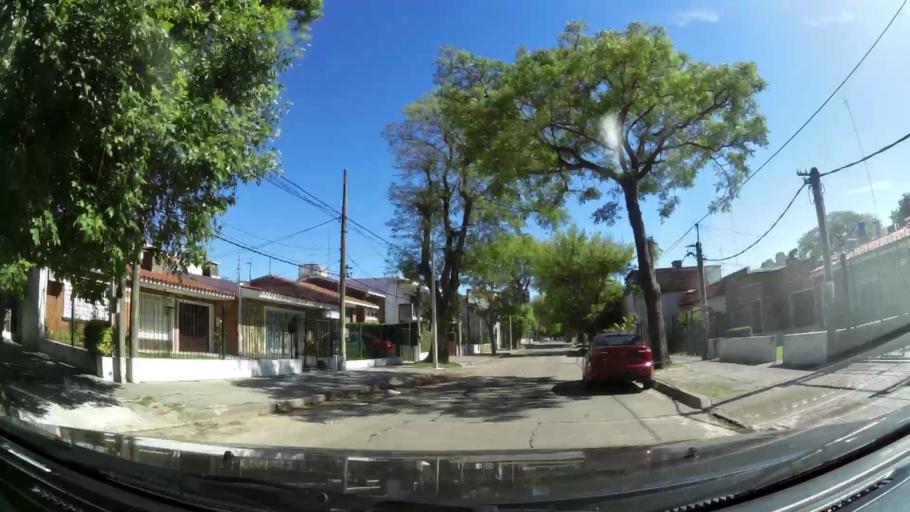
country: UY
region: Canelones
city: Paso de Carrasco
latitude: -34.8893
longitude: -56.1128
